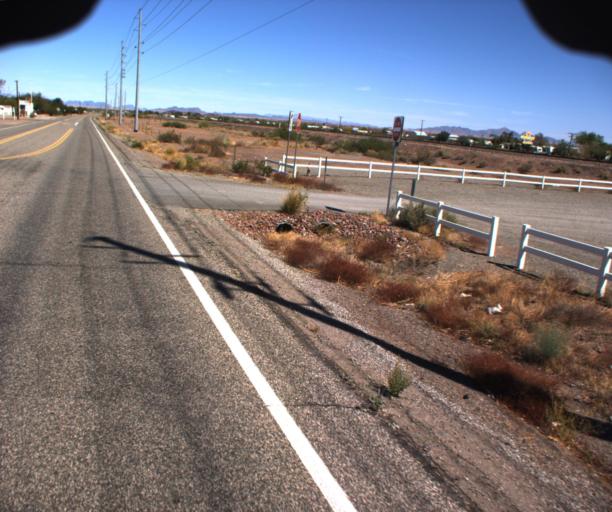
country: US
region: Arizona
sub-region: La Paz County
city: Cienega Springs
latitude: 33.9337
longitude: -114.0068
